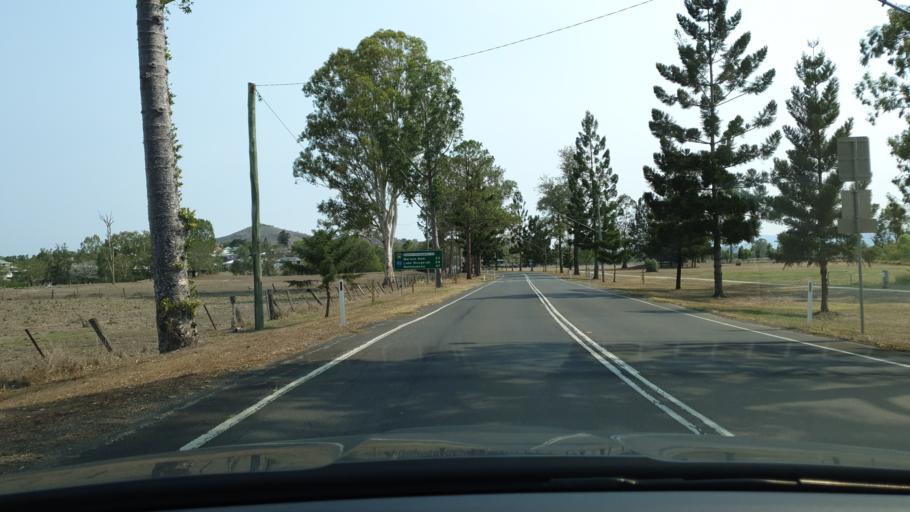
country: AU
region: Queensland
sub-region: Ipswich
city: Deebing Heights
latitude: -28.0012
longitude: 152.6819
